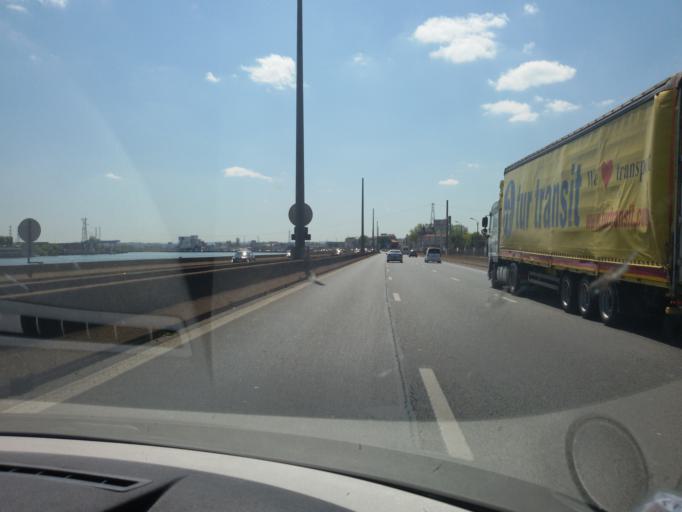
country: FR
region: Rhone-Alpes
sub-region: Departement du Rhone
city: La Mulatiere
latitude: 45.7237
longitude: 4.8175
